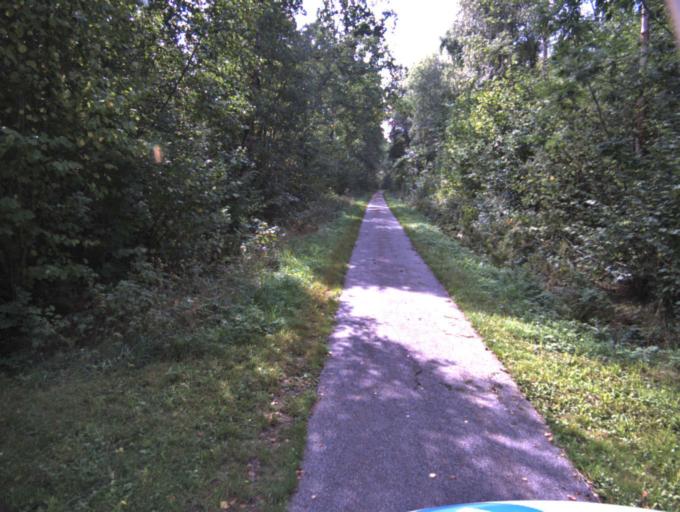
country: SE
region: Vaestra Goetaland
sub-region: Tranemo Kommun
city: Limmared
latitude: 57.6347
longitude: 13.3533
